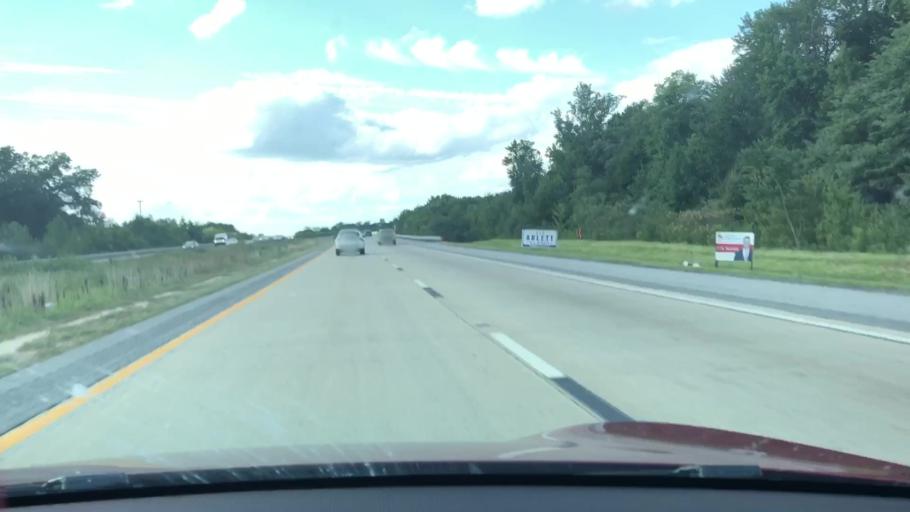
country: US
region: Delaware
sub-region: New Castle County
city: Townsend
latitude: 39.3642
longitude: -75.6546
